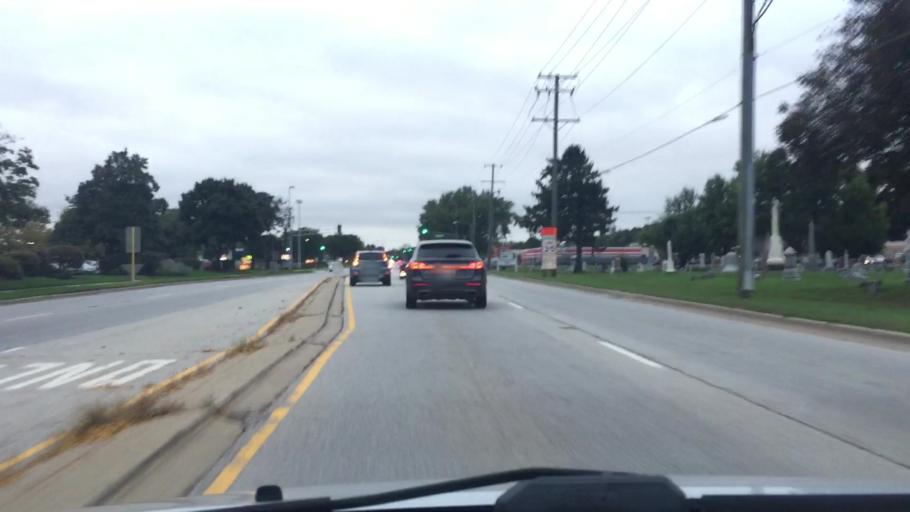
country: US
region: Illinois
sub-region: Kane County
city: West Dundee
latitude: 42.1025
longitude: -88.2890
